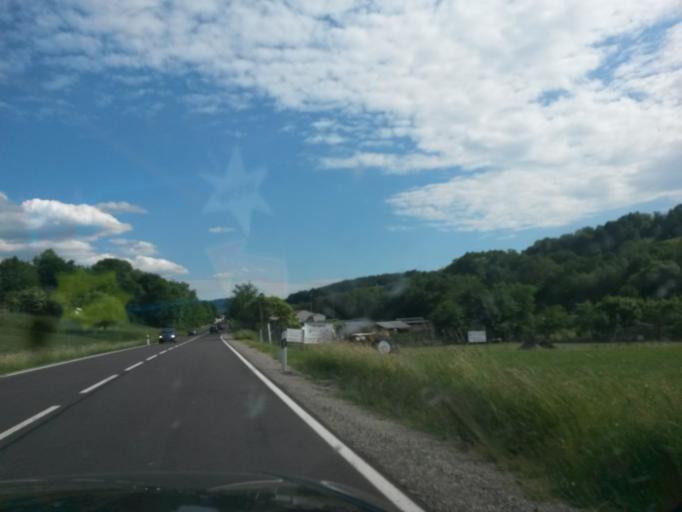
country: DE
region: Hesse
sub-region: Regierungsbezirk Kassel
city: Hilders
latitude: 50.5778
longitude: 9.9959
